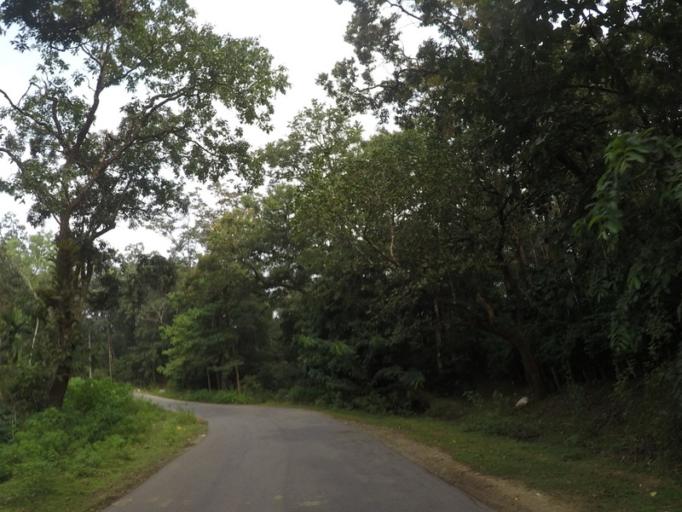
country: IN
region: Karnataka
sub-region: Chikmagalur
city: Koppa
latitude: 13.3629
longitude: 75.5054
